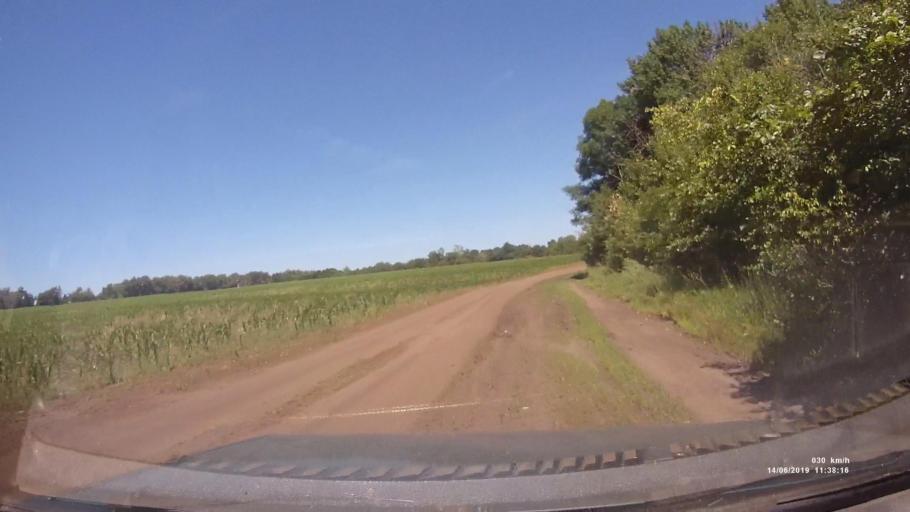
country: RU
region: Rostov
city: Kazanskaya
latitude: 49.8659
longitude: 41.3705
